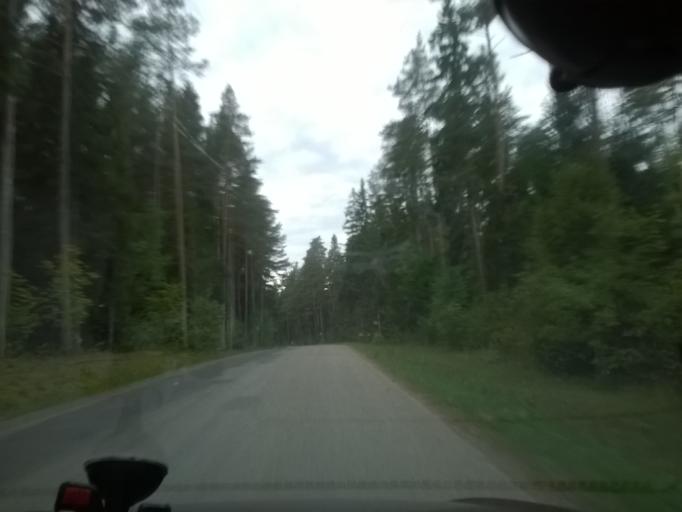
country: EE
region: Vorumaa
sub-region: Voru linn
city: Voru
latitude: 57.8165
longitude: 27.1137
